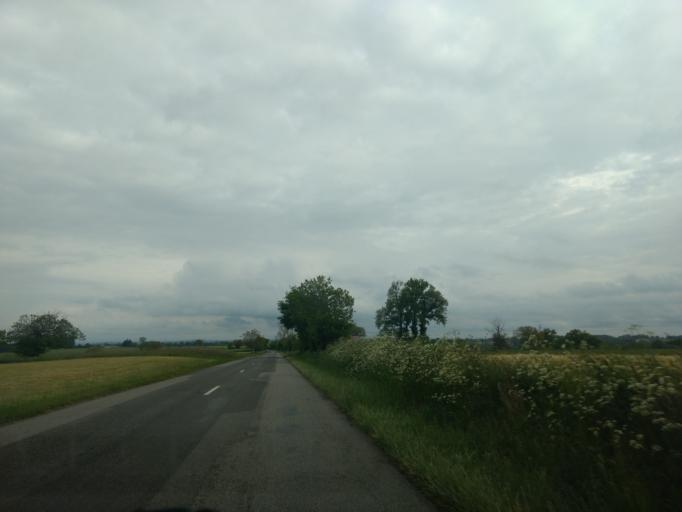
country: FR
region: Midi-Pyrenees
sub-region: Departement de l'Aveyron
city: Viviez
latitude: 44.5293
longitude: 2.1760
